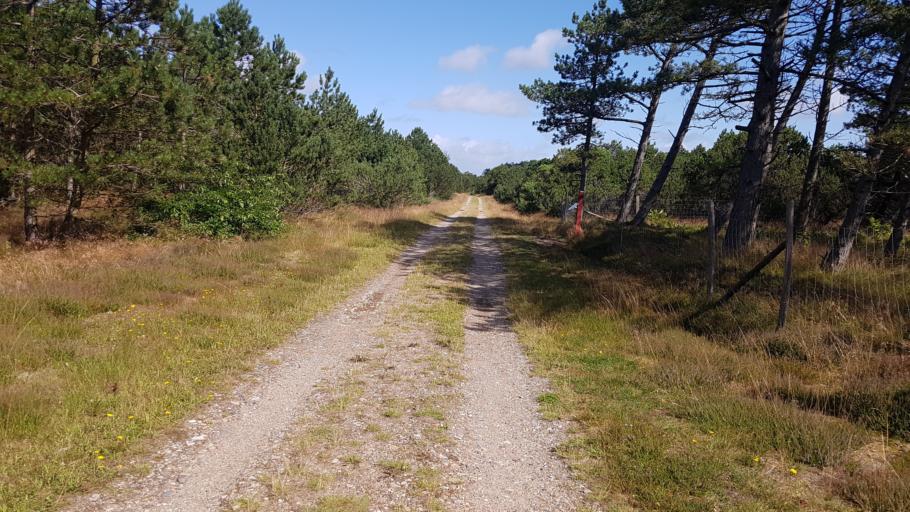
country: DE
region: Schleswig-Holstein
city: List
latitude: 55.1216
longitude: 8.5387
